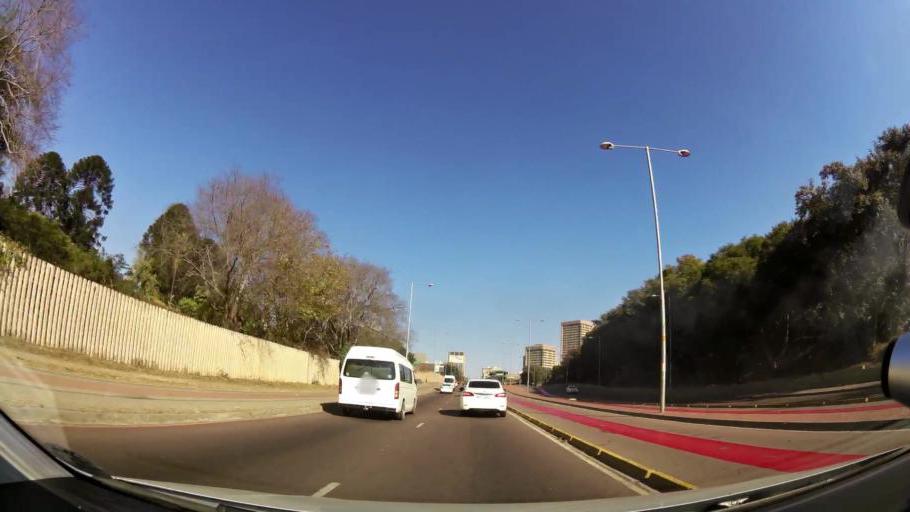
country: ZA
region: Gauteng
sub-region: City of Tshwane Metropolitan Municipality
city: Pretoria
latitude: -25.7369
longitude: 28.1873
